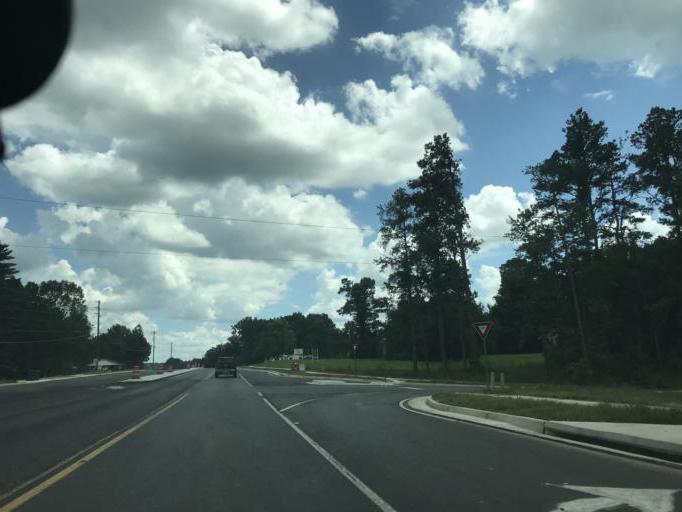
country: US
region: Georgia
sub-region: Forsyth County
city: Cumming
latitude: 34.2356
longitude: -84.1947
